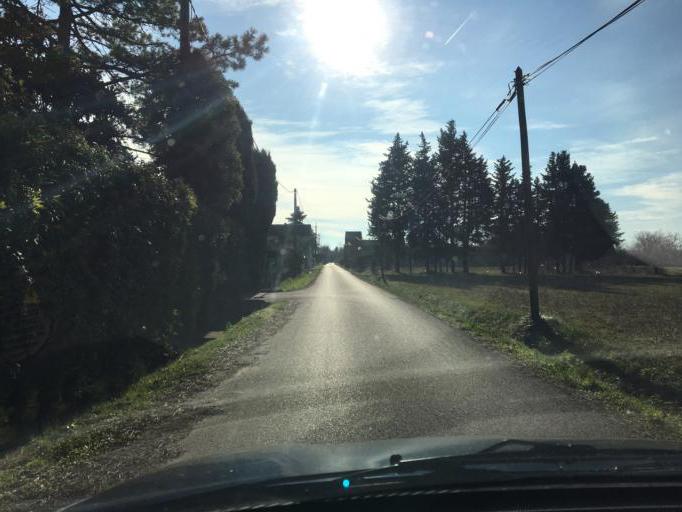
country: FR
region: Provence-Alpes-Cote d'Azur
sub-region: Departement du Vaucluse
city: Jonquieres
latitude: 44.1134
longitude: 4.8863
